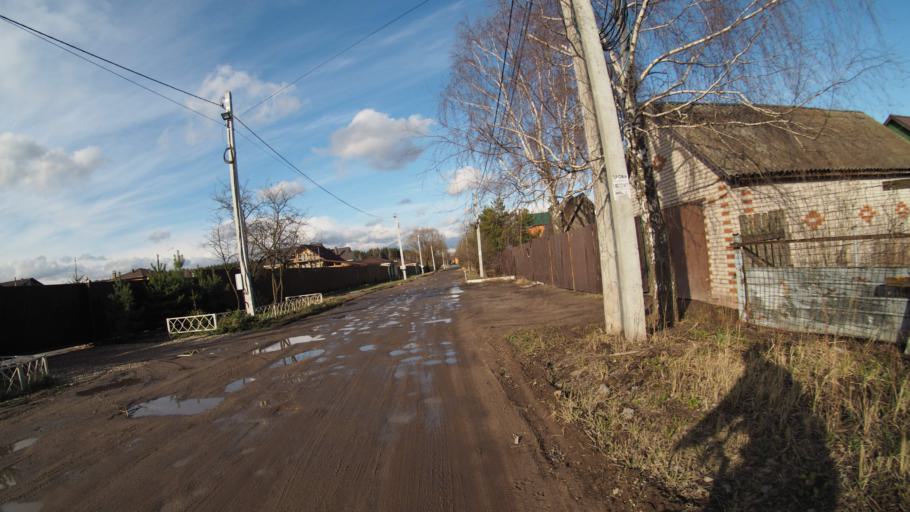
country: RU
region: Moskovskaya
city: Ramenskoye
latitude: 55.5578
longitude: 38.3060
